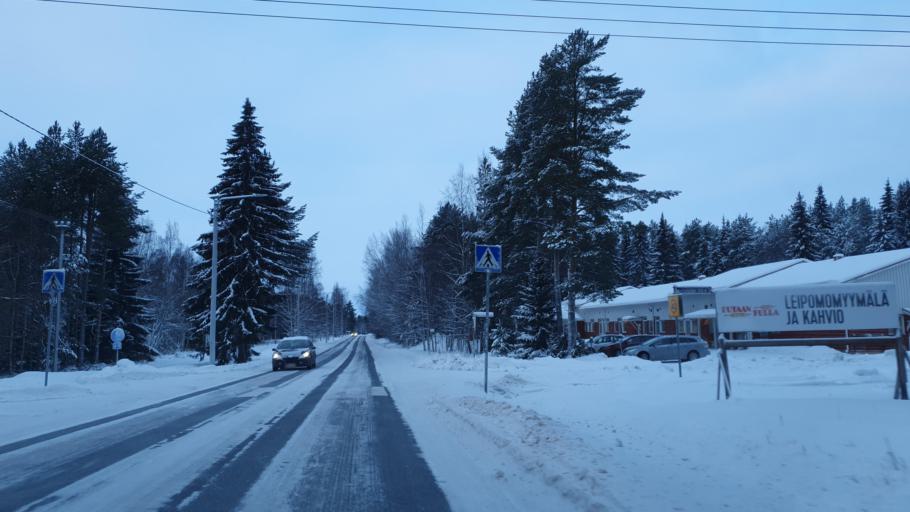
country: FI
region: Northern Ostrobothnia
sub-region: Oulu
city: Haukipudas
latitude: 65.2089
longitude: 25.3220
